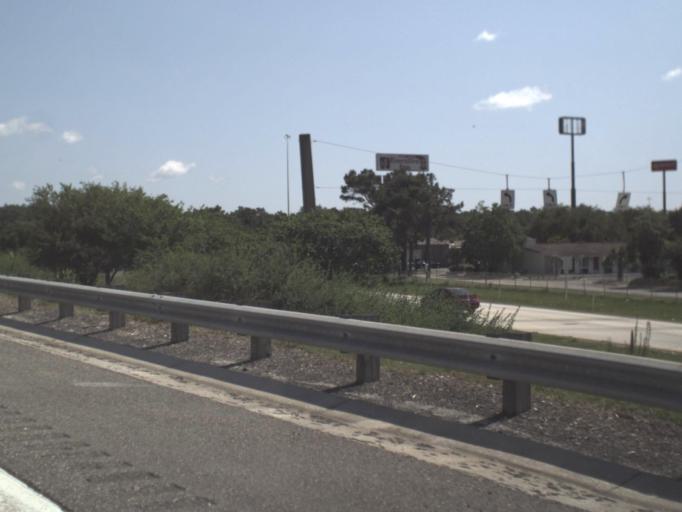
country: US
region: Florida
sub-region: Duval County
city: Jacksonville
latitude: 30.4282
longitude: -81.6561
